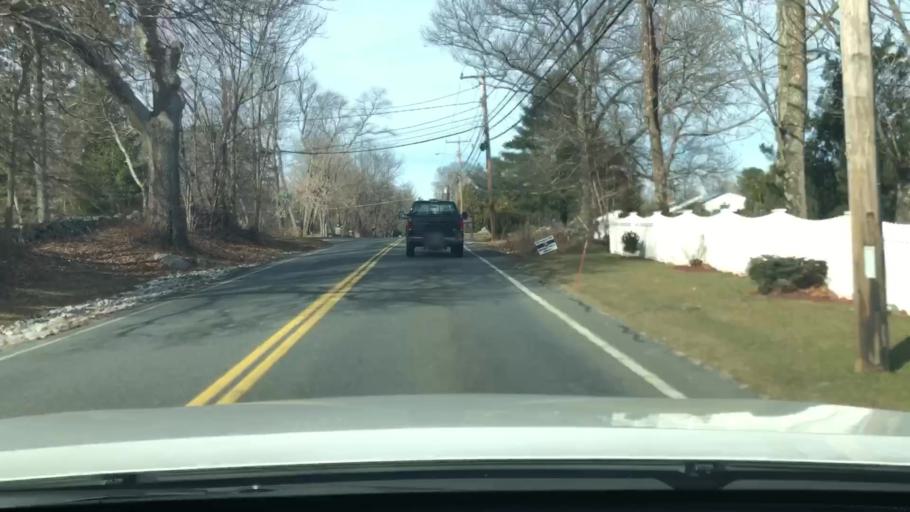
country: US
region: Massachusetts
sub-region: Worcester County
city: Mendon
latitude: 42.0885
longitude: -71.5326
